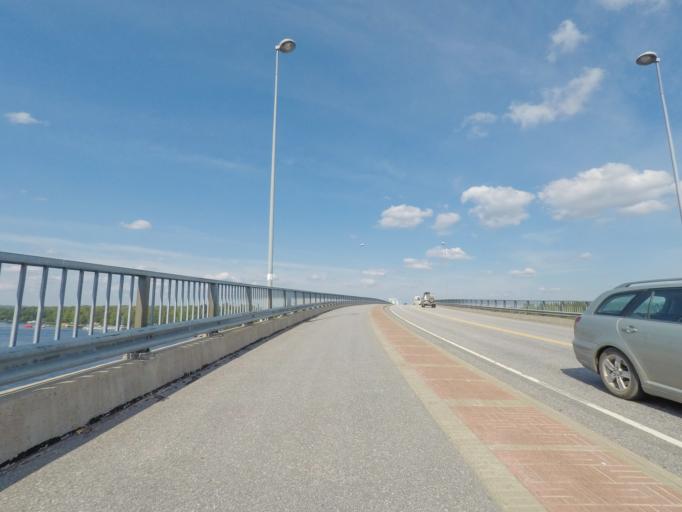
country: FI
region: Southern Savonia
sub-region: Mikkeli
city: Puumala
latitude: 61.5177
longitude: 28.1740
